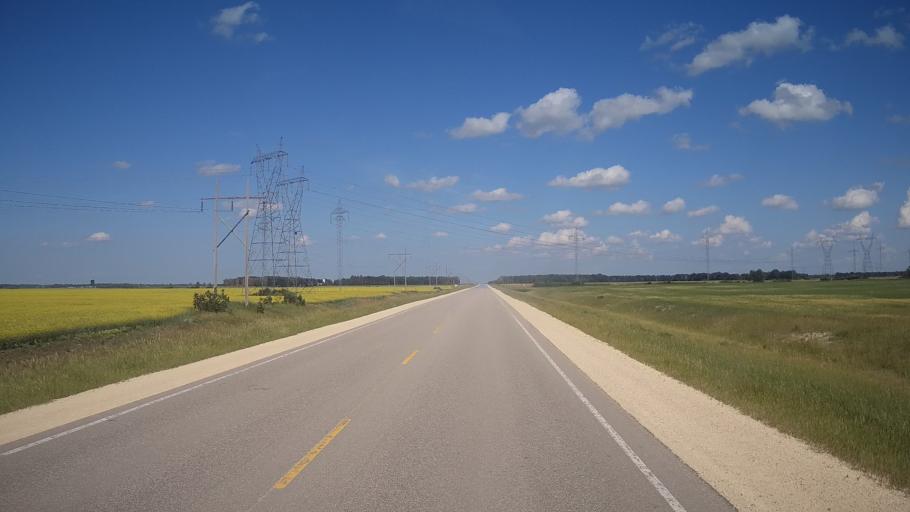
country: CA
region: Manitoba
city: Stonewall
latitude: 50.1226
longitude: -97.4941
